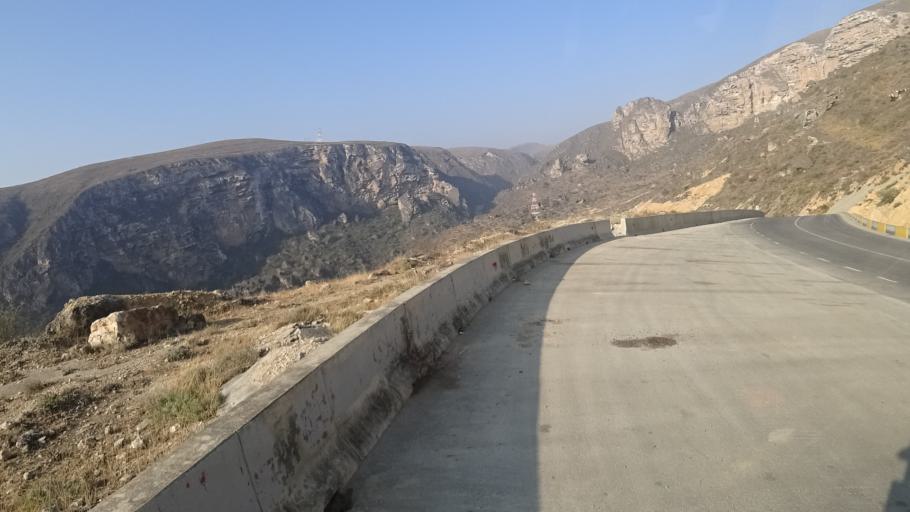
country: YE
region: Al Mahrah
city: Hawf
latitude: 16.7515
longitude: 53.2164
